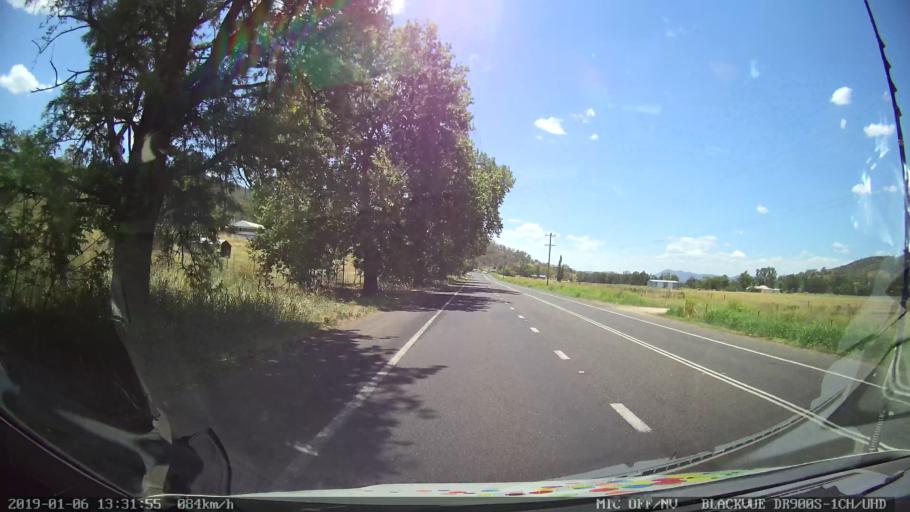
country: AU
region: New South Wales
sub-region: Tamworth Municipality
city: East Tamworth
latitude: -31.1162
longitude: 150.9961
